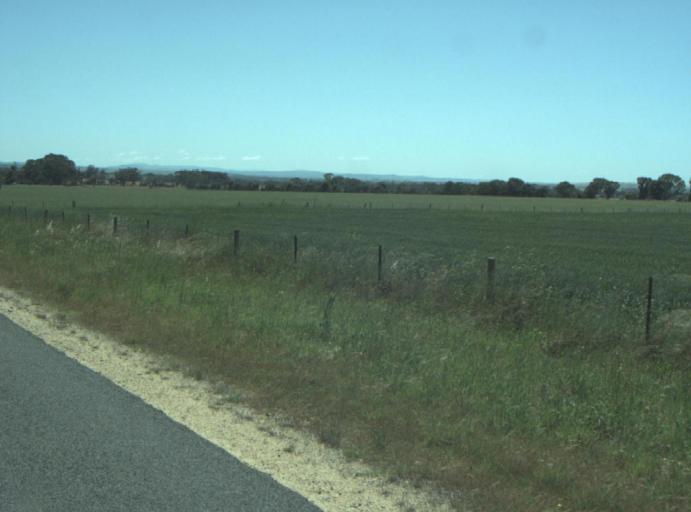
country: AU
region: Victoria
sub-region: Greater Geelong
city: Lara
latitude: -37.8602
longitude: 144.2798
